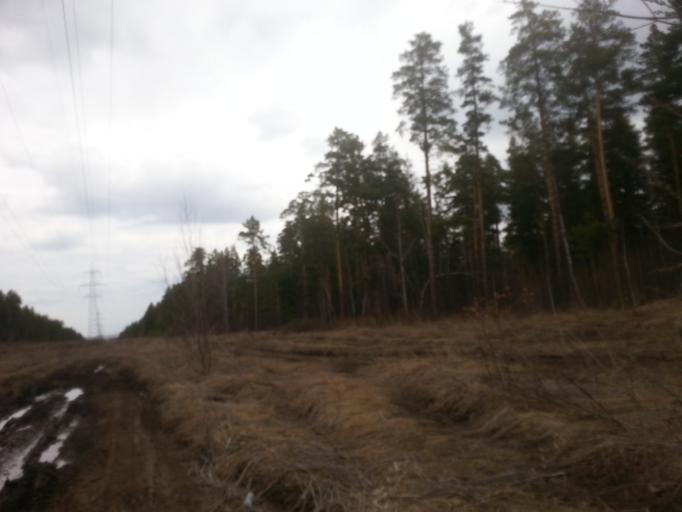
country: RU
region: Altai Krai
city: Yuzhnyy
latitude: 53.2894
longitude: 83.7276
